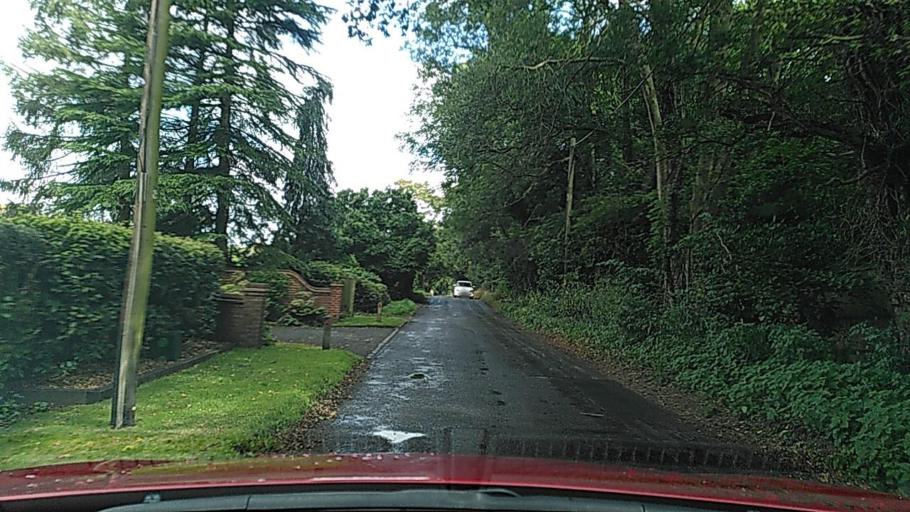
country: GB
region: England
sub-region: Wokingham
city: Sonning
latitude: 51.5063
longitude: -0.9315
